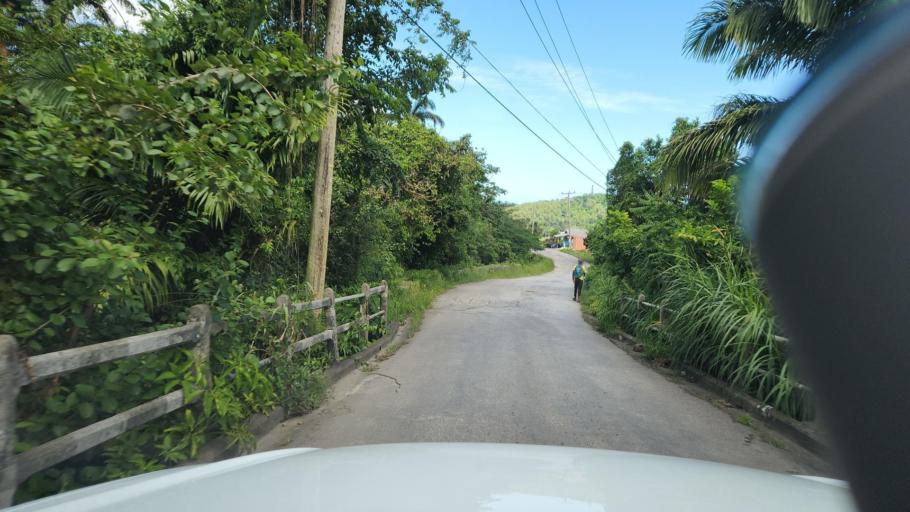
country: BB
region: Saint Thomas
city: Welchman Hall
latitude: 13.2053
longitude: -59.5585
